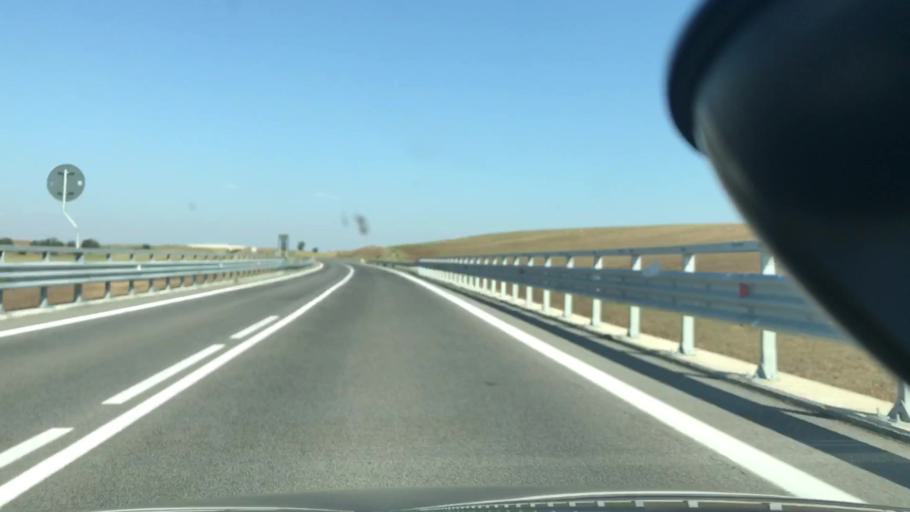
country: IT
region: Basilicate
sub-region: Provincia di Potenza
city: Palazzo San Gervasio
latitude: 40.9631
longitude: 16.0110
